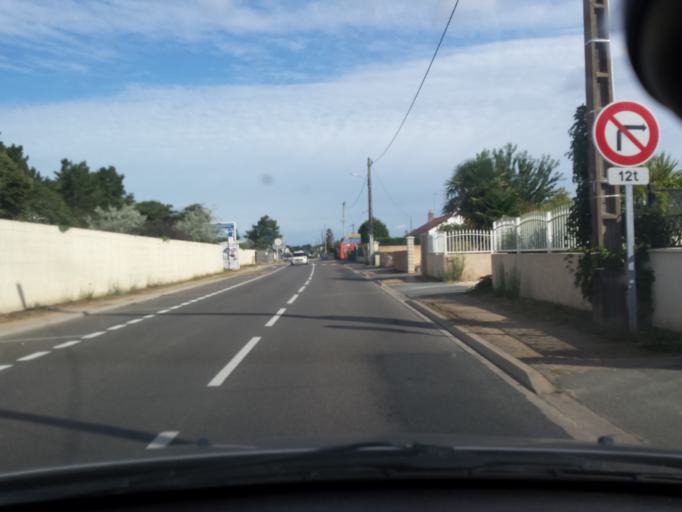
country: FR
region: Pays de la Loire
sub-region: Departement de la Vendee
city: Olonne-sur-Mer
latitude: 46.5452
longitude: -1.8030
